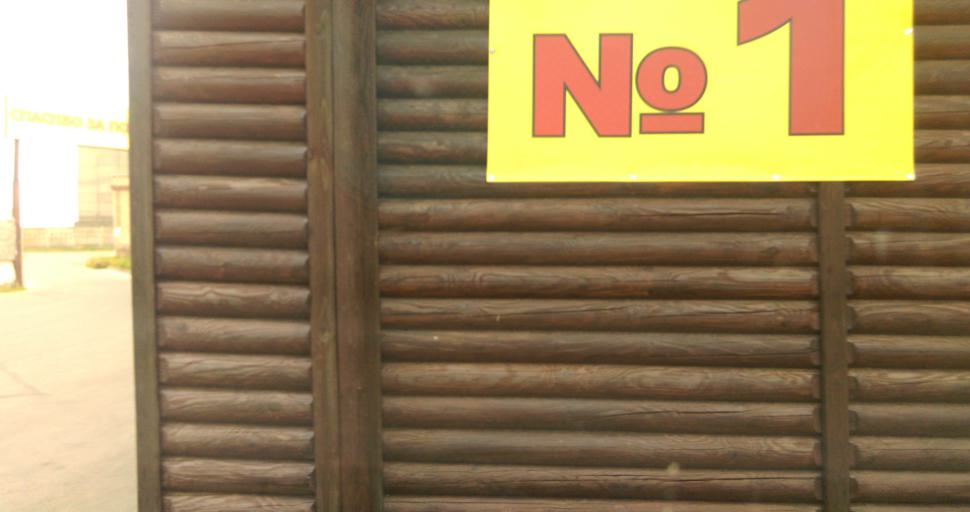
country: RU
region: Moskovskaya
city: Zhitnevo
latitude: 55.3351
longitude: 37.8958
